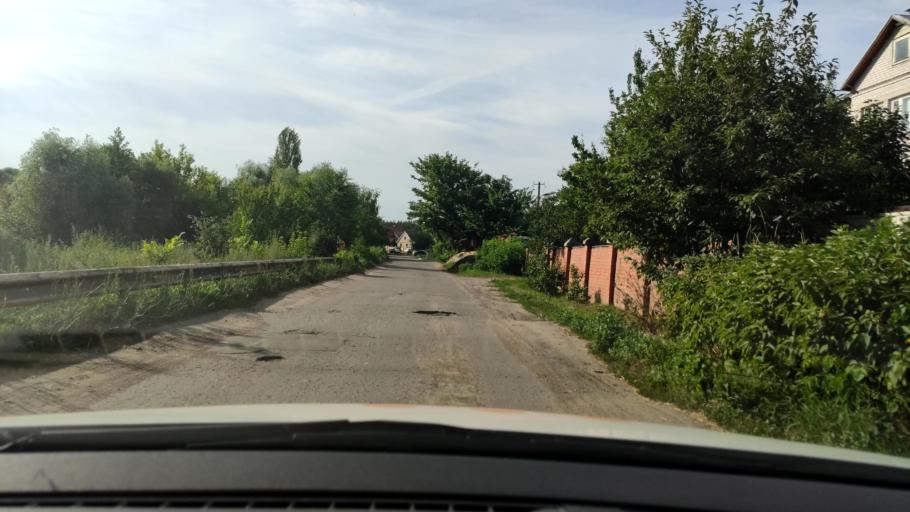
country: RU
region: Voronezj
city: Novaya Usman'
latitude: 51.6265
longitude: 39.4230
